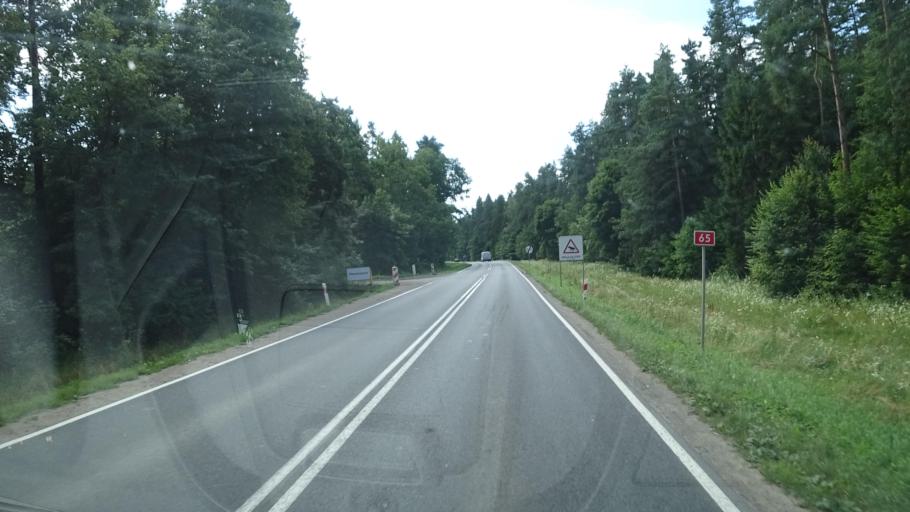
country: PL
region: Warmian-Masurian Voivodeship
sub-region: Powiat elcki
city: Elk
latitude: 53.7929
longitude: 22.3540
